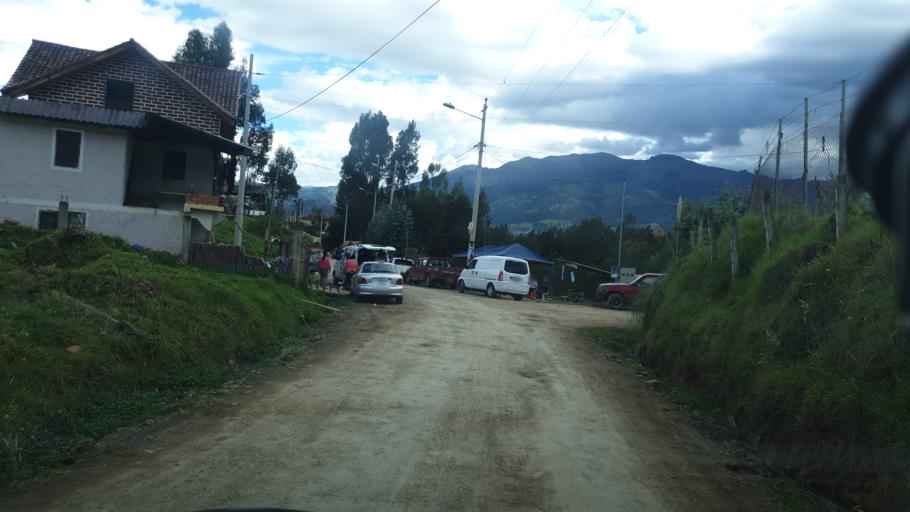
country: EC
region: Azuay
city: Cuenca
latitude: -2.8583
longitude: -79.0431
